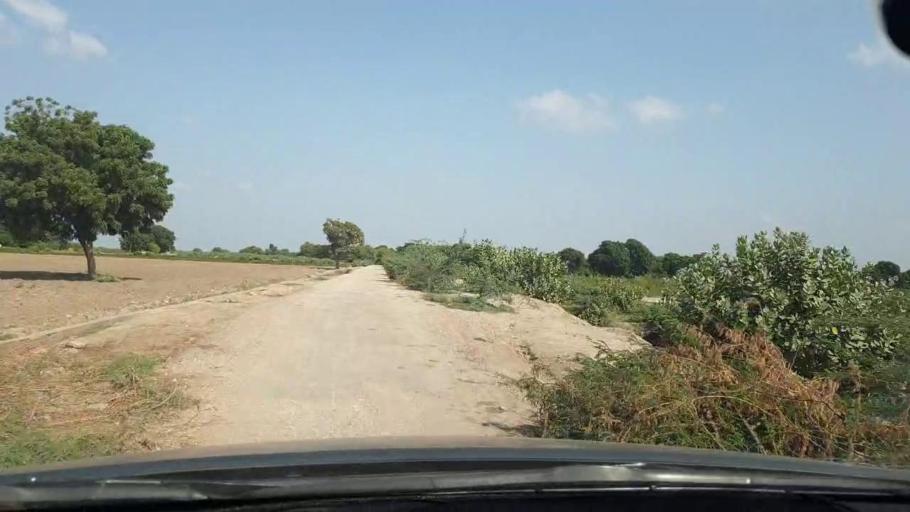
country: PK
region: Sindh
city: Naukot
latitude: 24.8886
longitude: 69.2778
